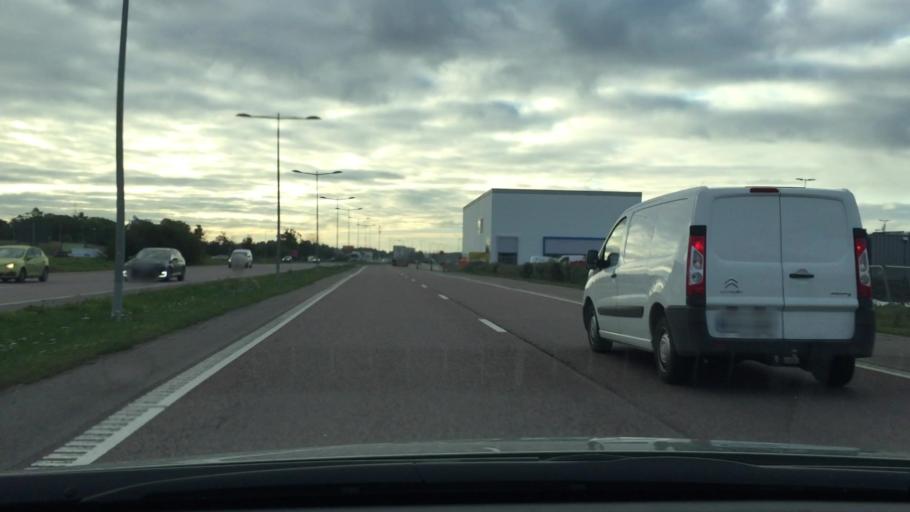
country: SE
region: Uppsala
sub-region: Uppsala Kommun
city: Saevja
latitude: 59.8520
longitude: 17.6904
